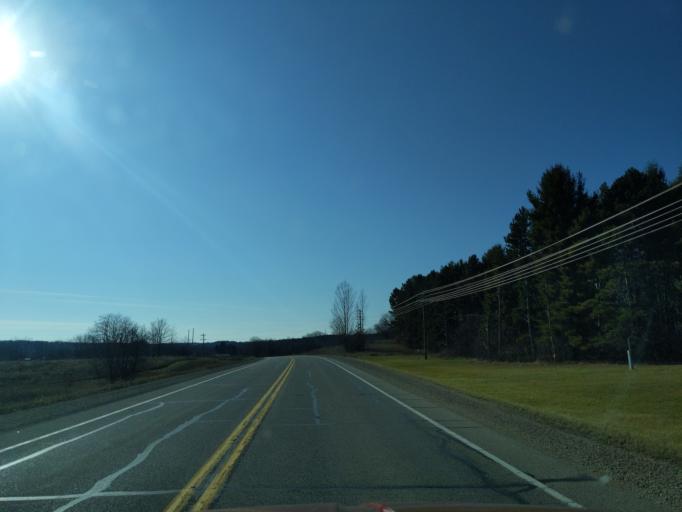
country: US
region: Wisconsin
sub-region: Waushara County
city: Wautoma
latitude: 44.1068
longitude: -89.2857
